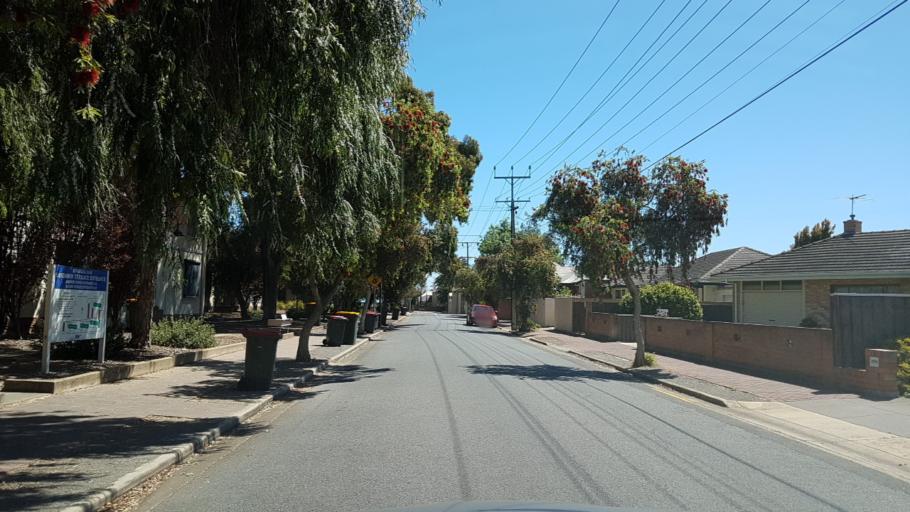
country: AU
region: South Australia
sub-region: Holdfast Bay
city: Glenelg East
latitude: -34.9748
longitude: 138.5235
